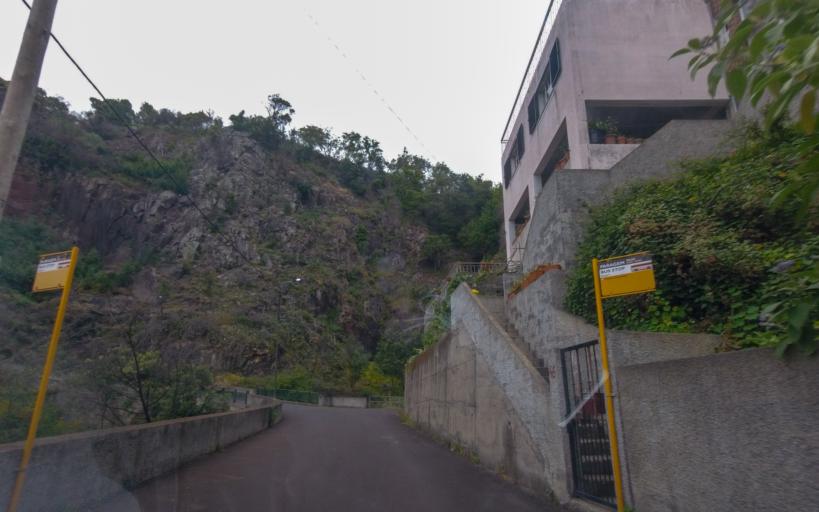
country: PT
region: Madeira
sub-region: Funchal
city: Nossa Senhora do Monte
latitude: 32.6749
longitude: -16.9116
